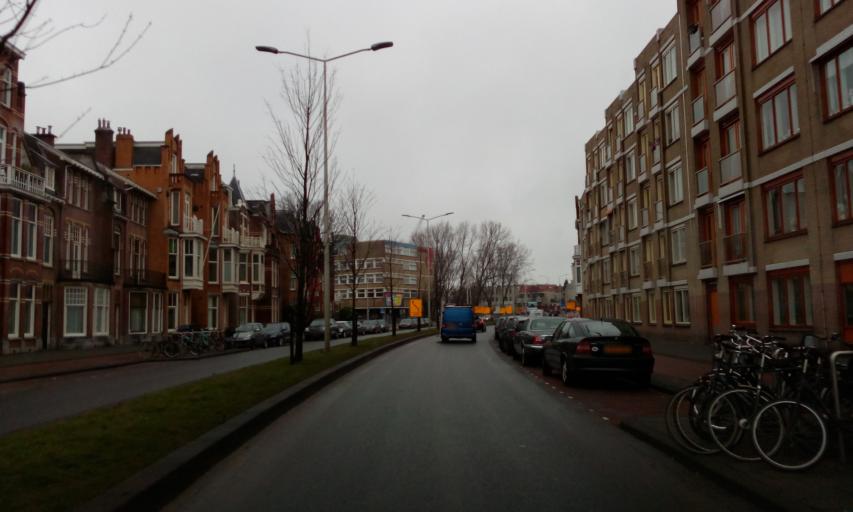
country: NL
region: South Holland
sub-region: Gemeente Den Haag
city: The Hague
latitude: 52.0804
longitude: 4.2763
